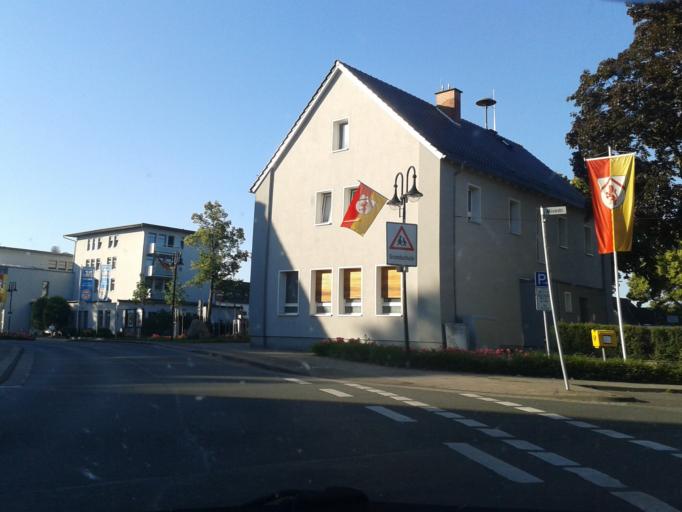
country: DE
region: North Rhine-Westphalia
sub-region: Regierungsbezirk Detmold
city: Paderborn
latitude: 51.7348
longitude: 8.6828
